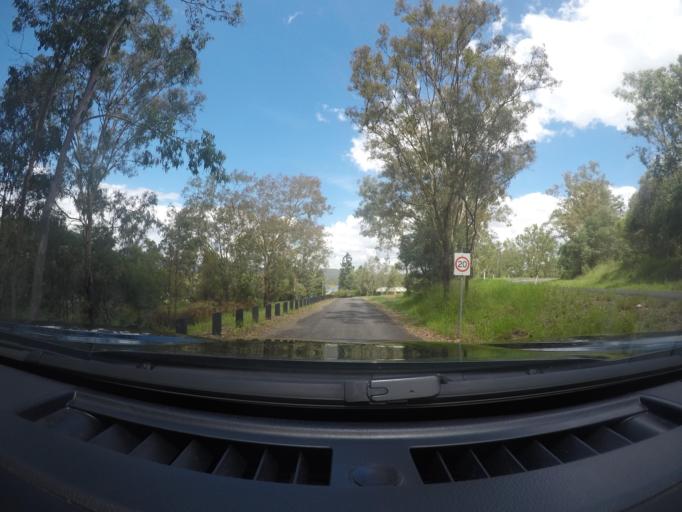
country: AU
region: Queensland
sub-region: Moreton Bay
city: Woodford
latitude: -27.1029
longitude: 152.5599
